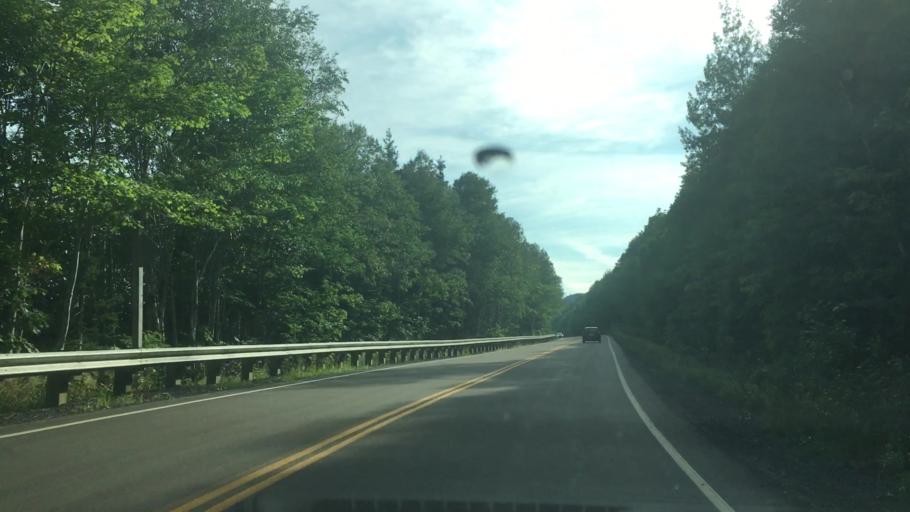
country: CA
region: Nova Scotia
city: Sydney Mines
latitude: 46.8265
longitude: -60.6222
